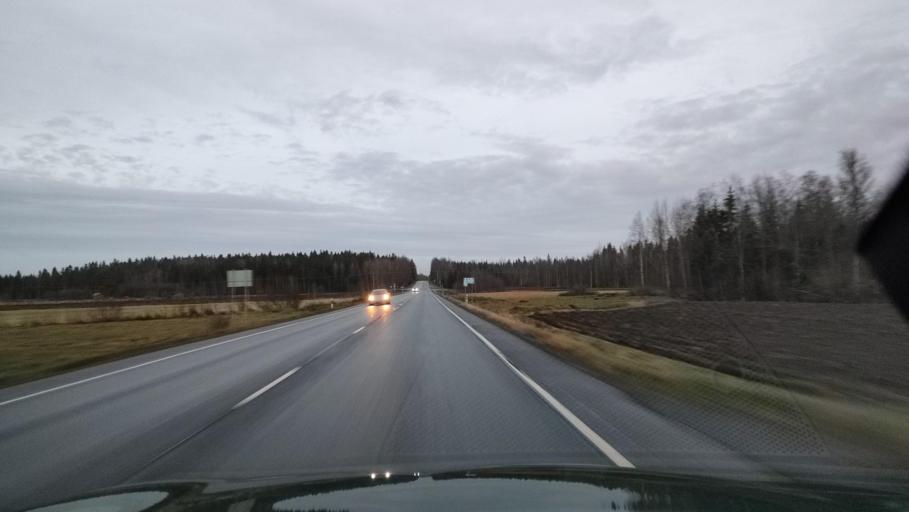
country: FI
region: Ostrobothnia
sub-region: Vaasa
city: Ristinummi
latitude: 62.9897
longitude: 21.7668
